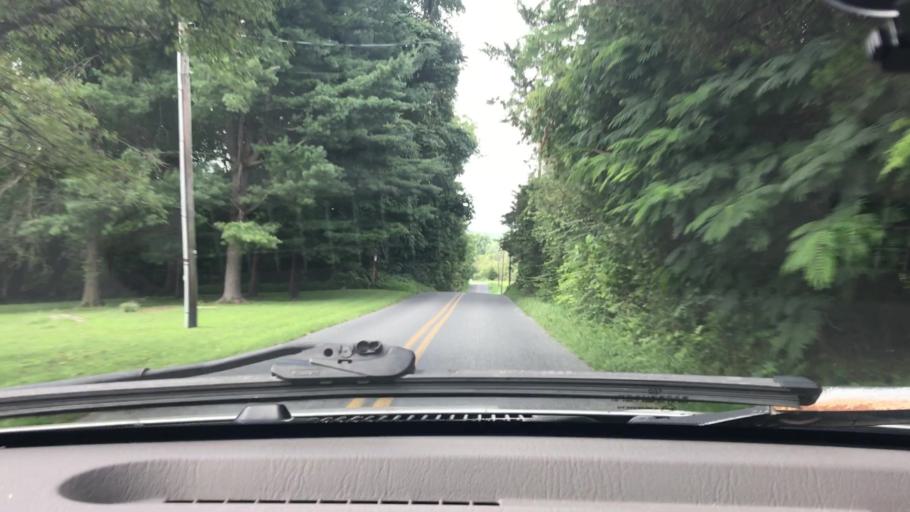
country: US
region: Pennsylvania
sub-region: Lancaster County
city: Elizabethtown
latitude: 40.1693
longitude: -76.6193
